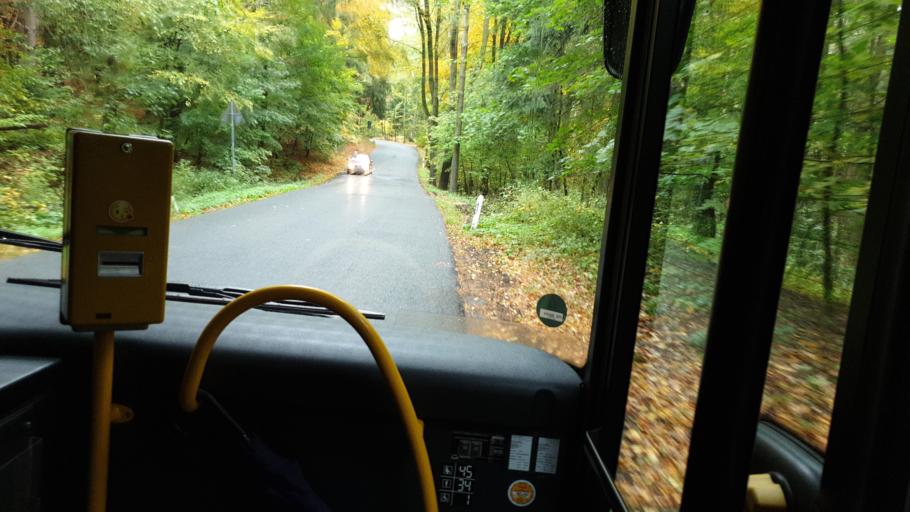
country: DE
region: Saxony
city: Kurort Gohrisch
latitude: 50.9021
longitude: 14.1162
